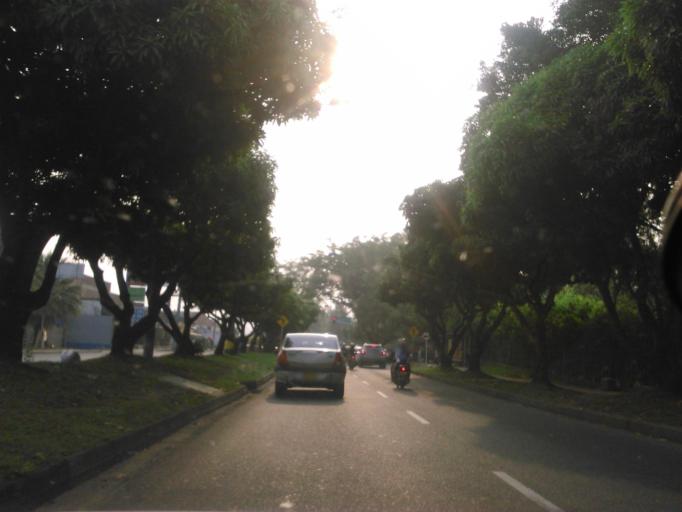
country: CO
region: Antioquia
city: Itagui
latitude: 6.2081
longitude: -75.5921
